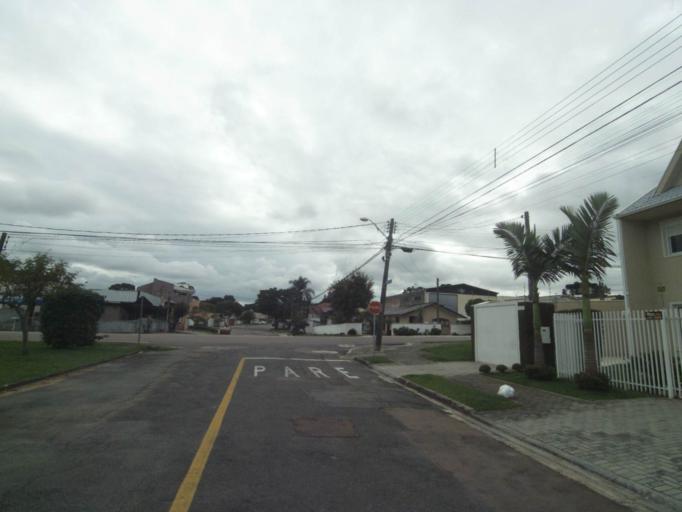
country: BR
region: Parana
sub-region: Curitiba
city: Curitiba
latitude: -25.4852
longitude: -49.2797
